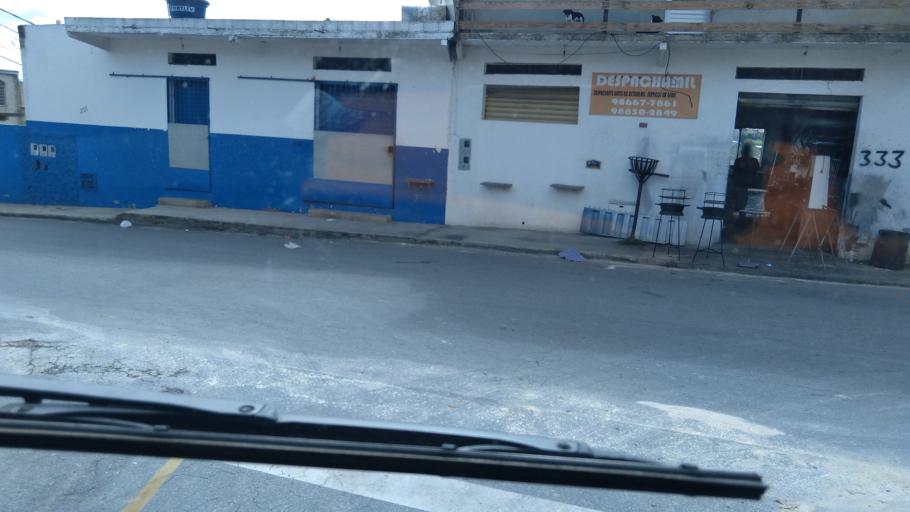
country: BR
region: Minas Gerais
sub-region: Santa Luzia
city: Santa Luzia
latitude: -19.8333
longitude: -43.8975
